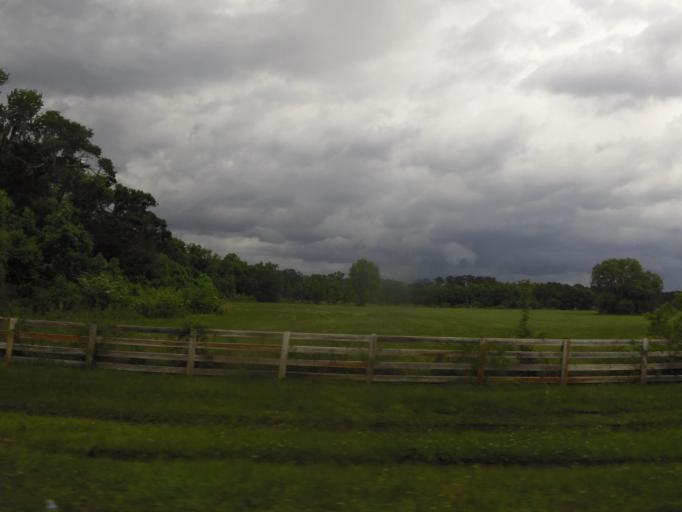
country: US
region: Florida
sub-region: Duval County
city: Jacksonville
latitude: 30.3462
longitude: -81.8010
